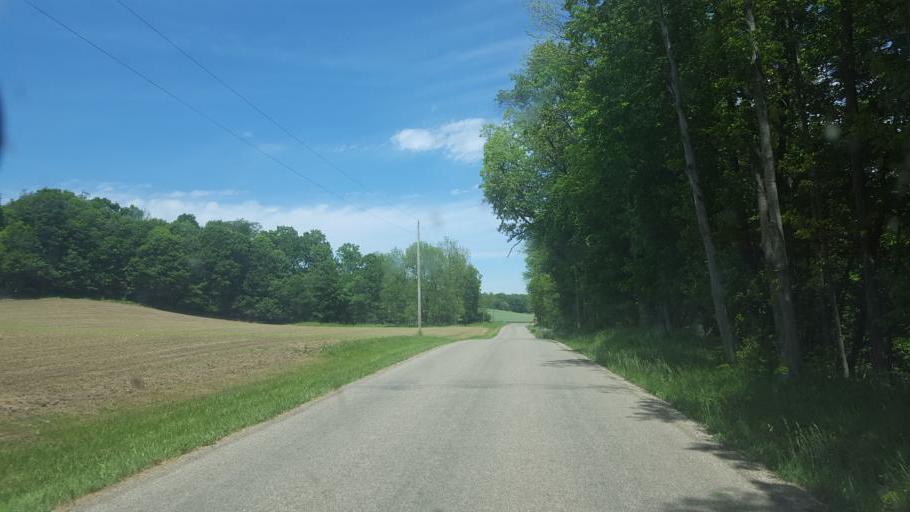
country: US
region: Ohio
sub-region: Knox County
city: Gambier
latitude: 40.3879
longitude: -82.3177
